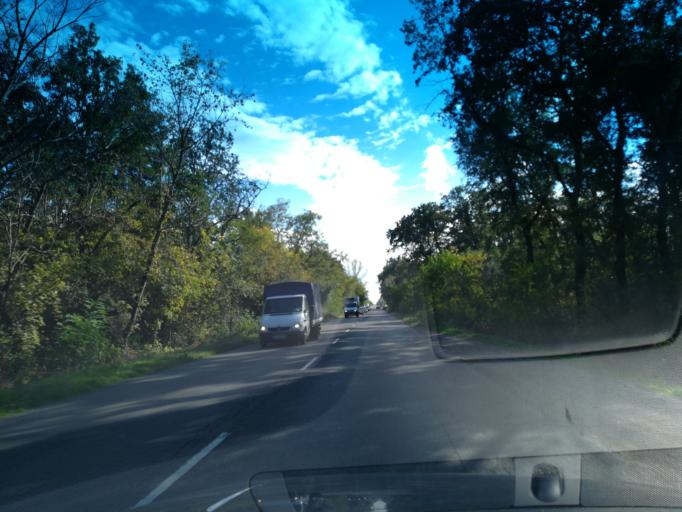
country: BG
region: Stara Zagora
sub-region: Obshtina Stara Zagora
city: Stara Zagora
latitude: 42.3527
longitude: 25.6581
